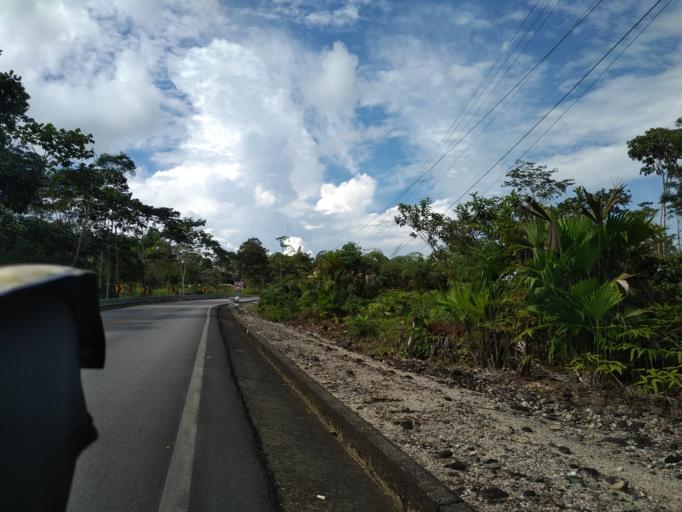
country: EC
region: Napo
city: Tena
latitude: -1.1072
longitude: -77.8051
